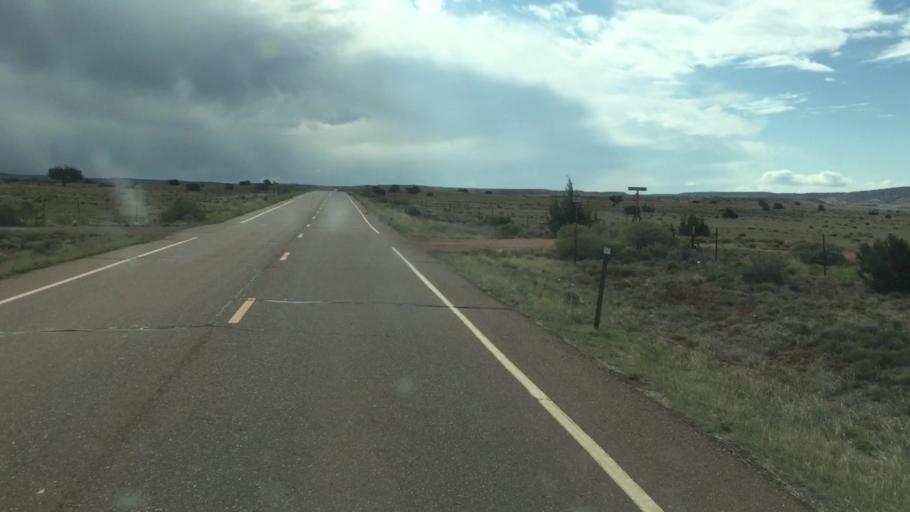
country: US
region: Arizona
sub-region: Apache County
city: Saint Johns
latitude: 34.5118
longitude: -109.6892
